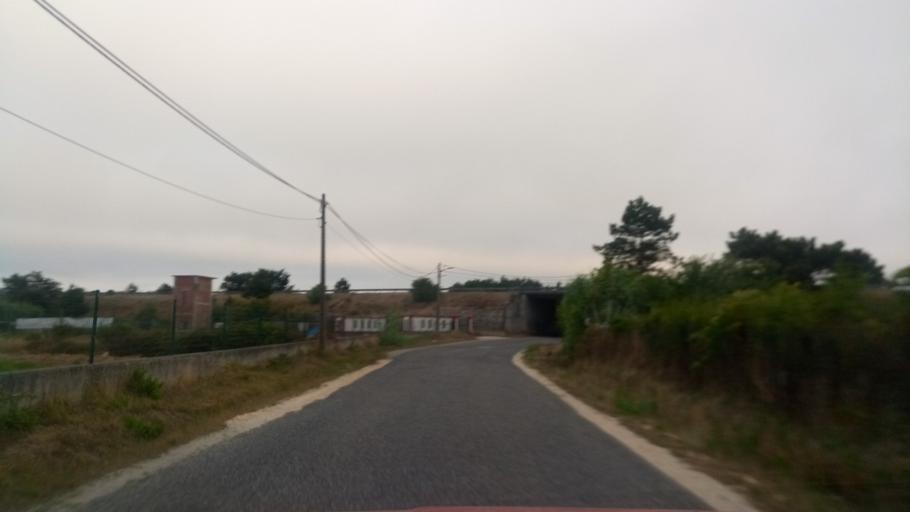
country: PT
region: Leiria
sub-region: Caldas da Rainha
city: Caldas da Rainha
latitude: 39.4221
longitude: -9.1500
